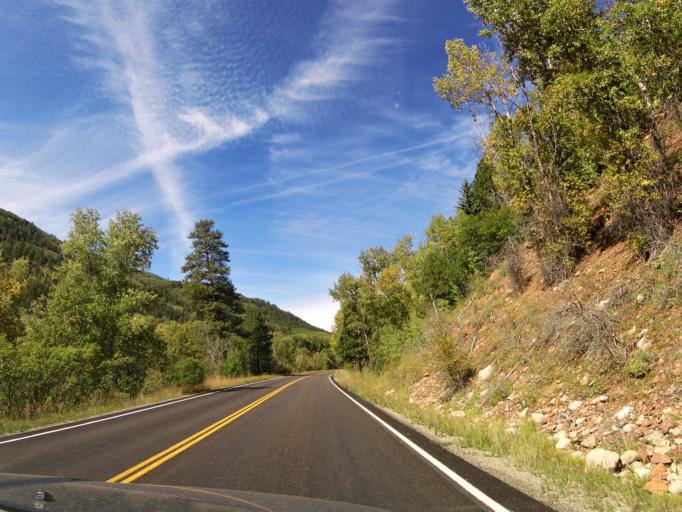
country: US
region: Colorado
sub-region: Montezuma County
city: Mancos
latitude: 37.5766
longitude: -108.1990
